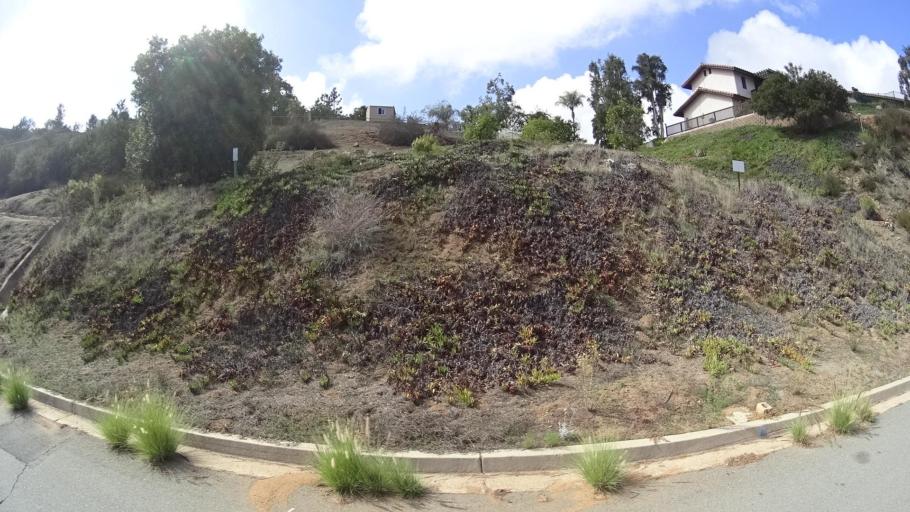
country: US
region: California
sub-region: San Diego County
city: Granite Hills
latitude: 32.7772
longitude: -116.8998
